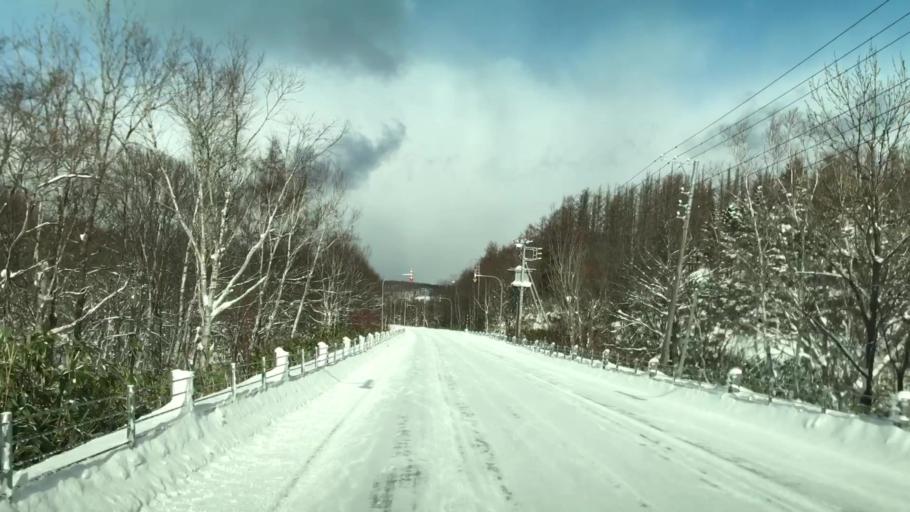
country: JP
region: Hokkaido
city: Yoichi
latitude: 43.2981
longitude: 140.5677
